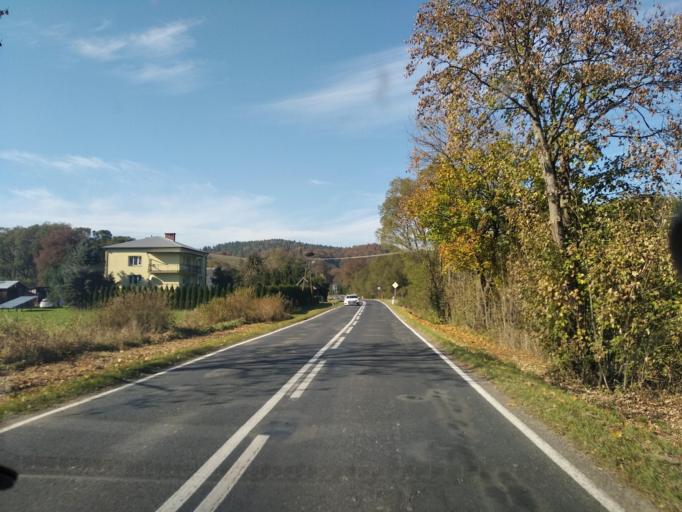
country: PL
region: Subcarpathian Voivodeship
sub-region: Powiat leski
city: Baligrod
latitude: 49.3585
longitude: 22.2811
